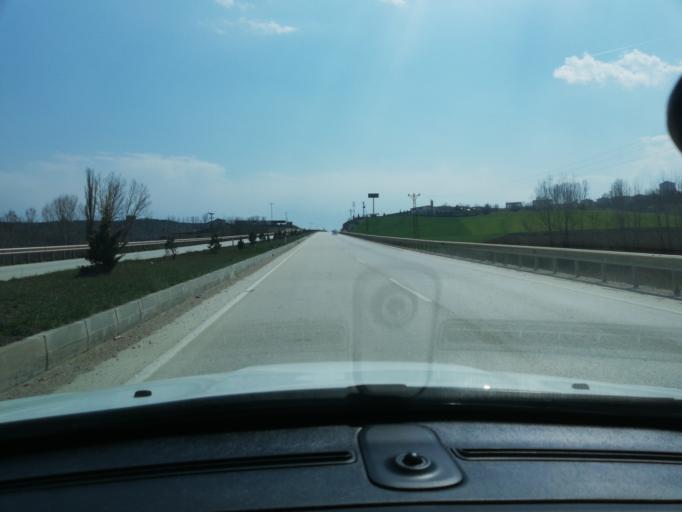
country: TR
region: Kastamonu
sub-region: Cide
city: Kastamonu
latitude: 41.4409
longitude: 33.7966
